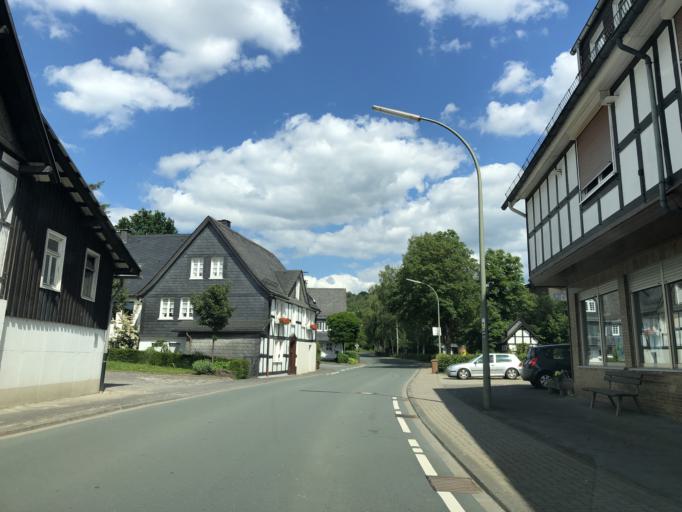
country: DE
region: North Rhine-Westphalia
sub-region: Regierungsbezirk Arnsberg
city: Schmallenberg
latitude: 51.1461
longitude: 8.3287
